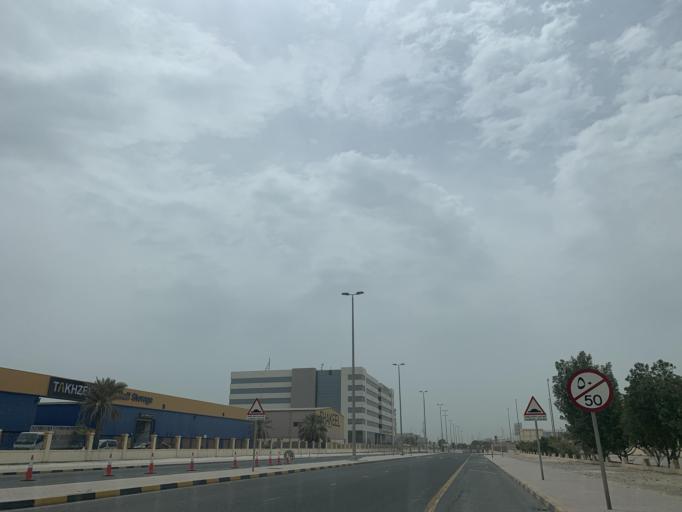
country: BH
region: Muharraq
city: Al Hadd
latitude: 26.2160
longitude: 50.6672
